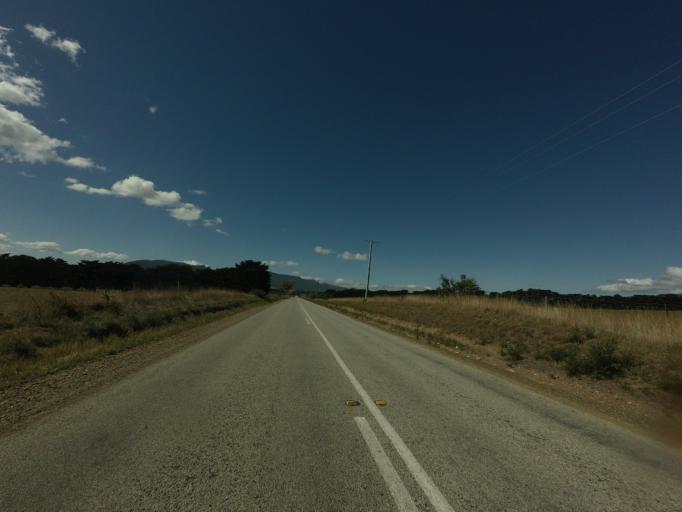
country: AU
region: Tasmania
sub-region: Break O'Day
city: St Helens
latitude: -41.6092
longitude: 148.0210
